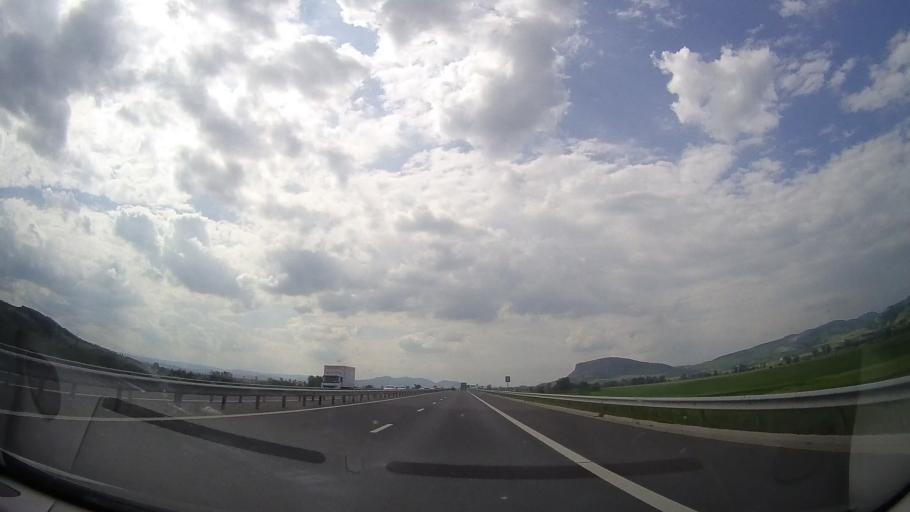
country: RO
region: Hunedoara
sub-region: Comuna Rapoltu Mare
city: Rapoltu Mare
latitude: 45.8418
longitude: 23.0810
